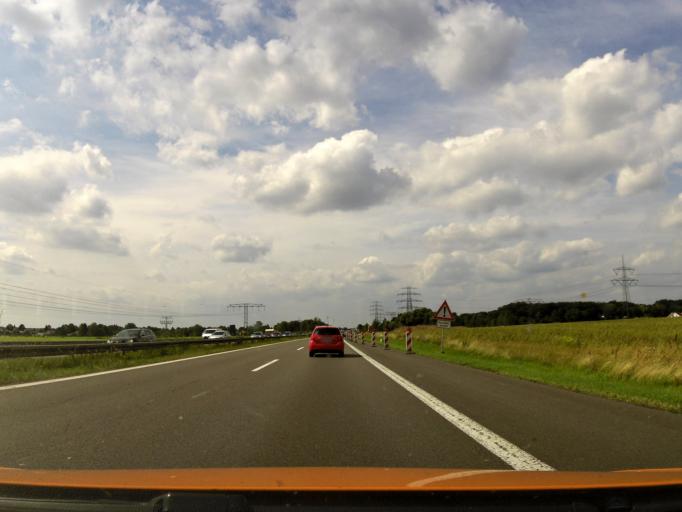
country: DE
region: Berlin
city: Buch
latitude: 52.6181
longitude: 13.5121
